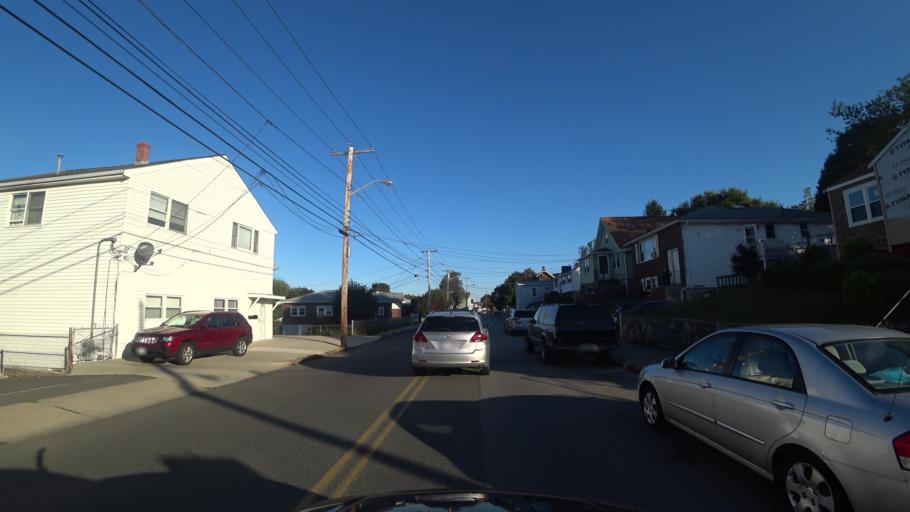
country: US
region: Massachusetts
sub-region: Suffolk County
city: Revere
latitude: 42.4197
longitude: -71.0133
